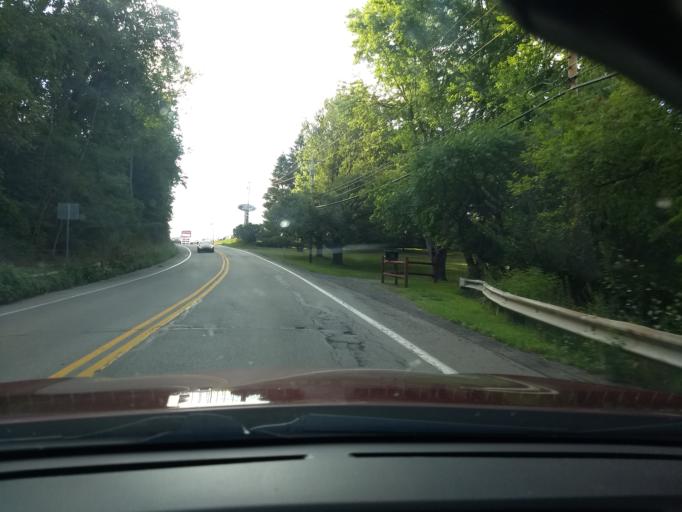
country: US
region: Pennsylvania
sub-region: Armstrong County
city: Freeport
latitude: 40.6660
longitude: -79.7048
